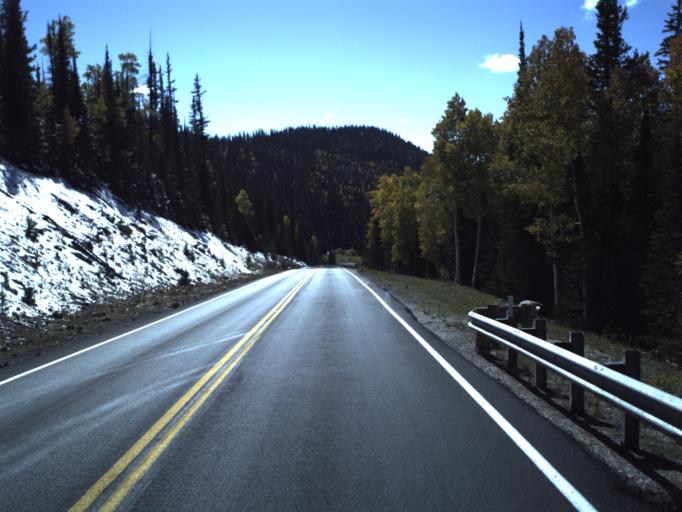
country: US
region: Utah
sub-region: Piute County
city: Junction
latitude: 38.3081
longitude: -112.4147
